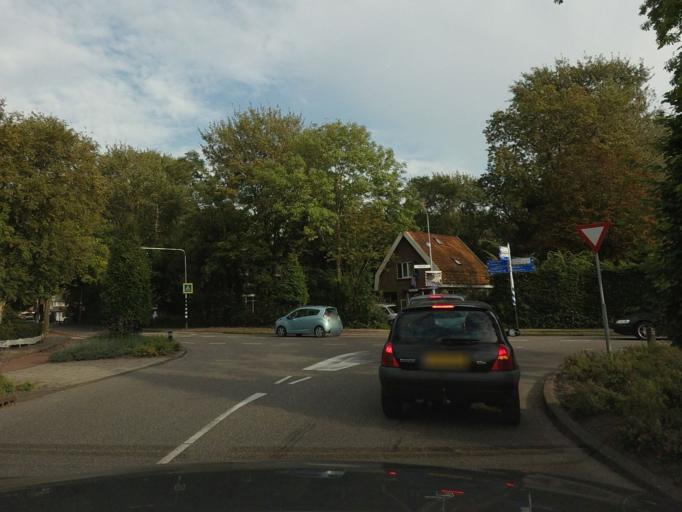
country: NL
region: North Holland
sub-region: Gemeente Schagen
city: Harenkarspel
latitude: 52.7046
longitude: 4.7053
